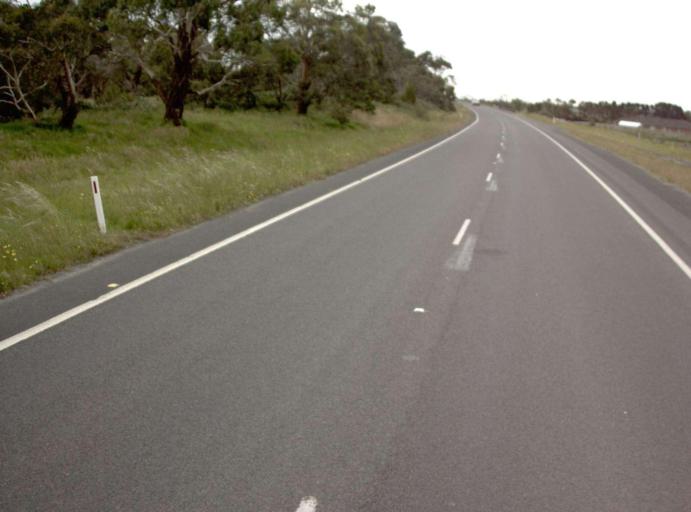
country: AU
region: Victoria
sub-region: Casey
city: Junction Village
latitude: -38.1490
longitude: 145.3153
